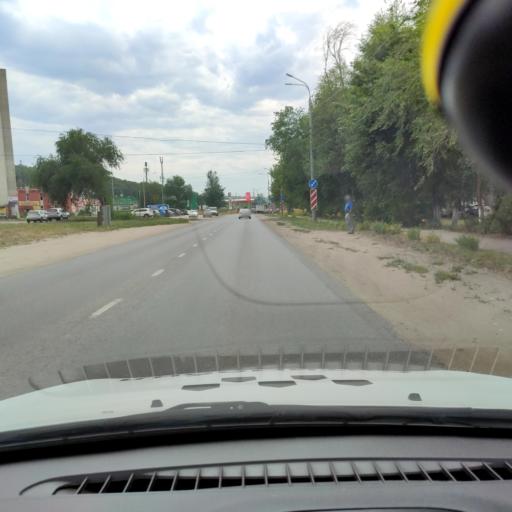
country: RU
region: Samara
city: Zhigulevsk
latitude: 53.4042
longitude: 49.5209
